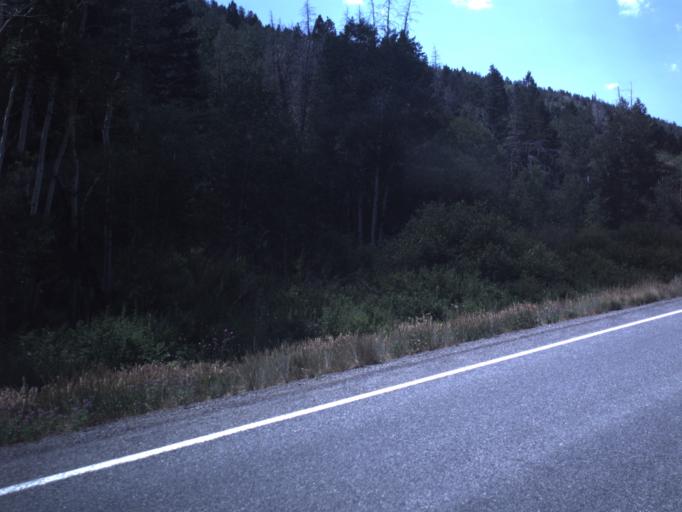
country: US
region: Utah
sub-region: Carbon County
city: Helper
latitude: 39.8574
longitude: -111.0628
